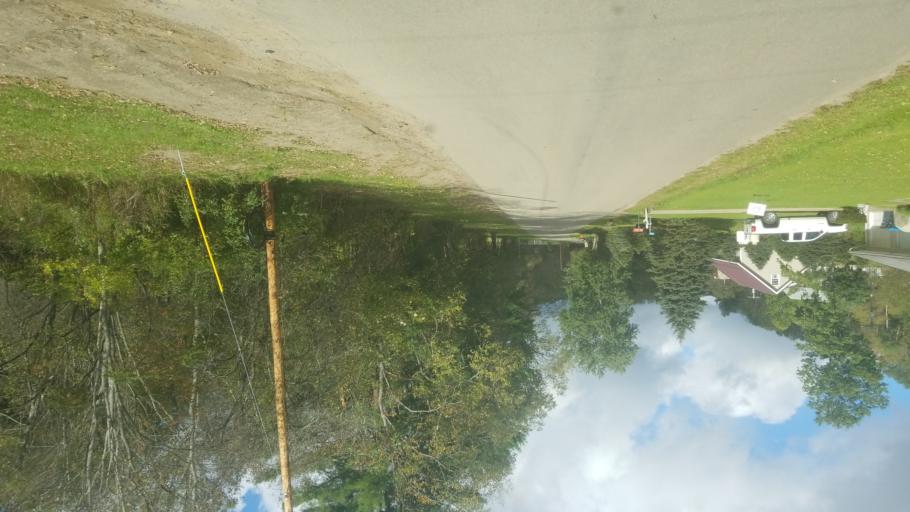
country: US
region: New York
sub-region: Cattaraugus County
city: Weston Mills
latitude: 42.1428
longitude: -78.3503
